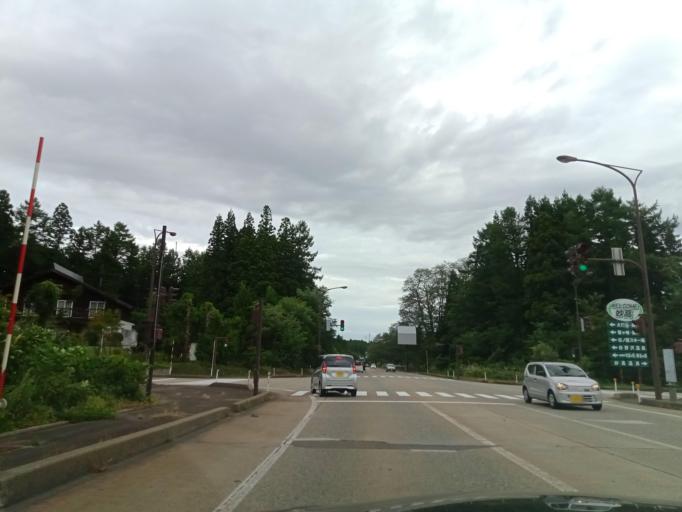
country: JP
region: Niigata
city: Arai
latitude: 36.8608
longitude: 138.1954
